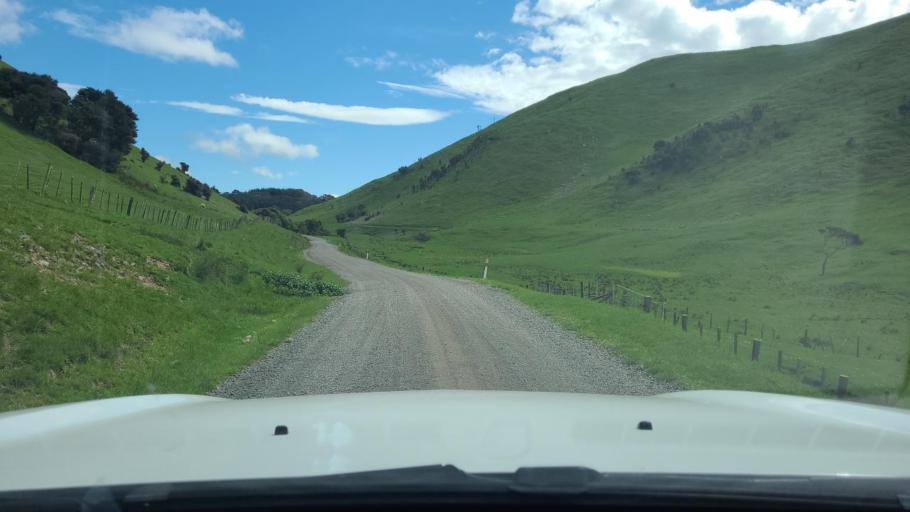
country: NZ
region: Wellington
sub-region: South Wairarapa District
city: Waipawa
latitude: -41.3248
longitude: 175.3895
